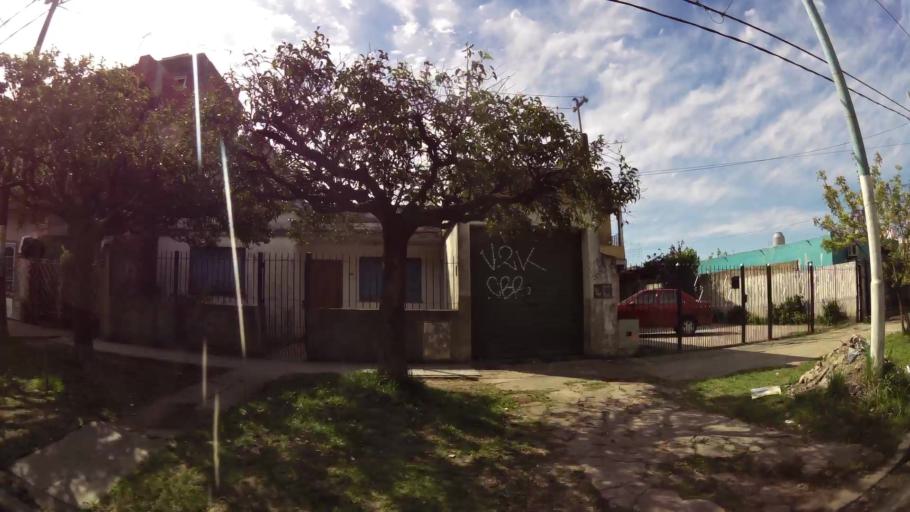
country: AR
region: Buenos Aires
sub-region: Partido de Quilmes
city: Quilmes
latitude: -34.7741
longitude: -58.2921
